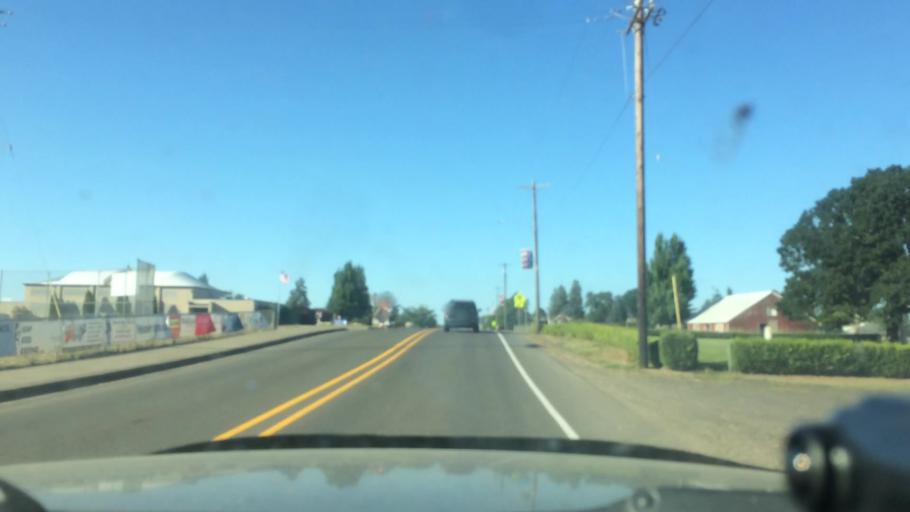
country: US
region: Oregon
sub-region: Yamhill County
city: Dundee
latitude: 45.2123
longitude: -122.9758
